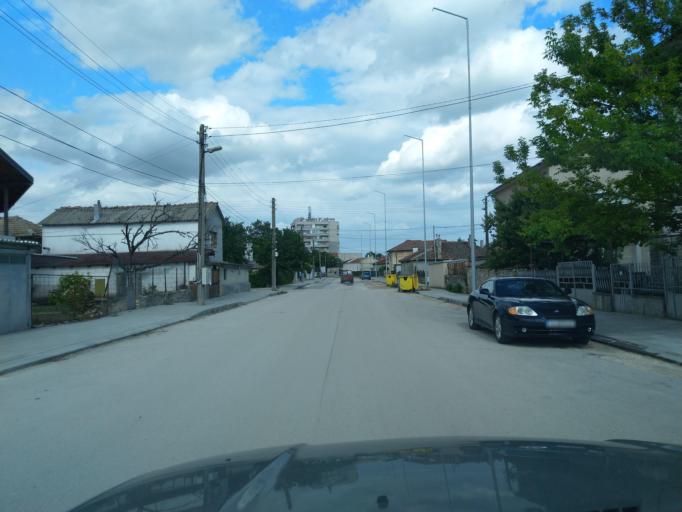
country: BG
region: Dobrich
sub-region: Obshtina Kavarna
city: Kavarna
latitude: 43.4301
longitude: 28.3332
